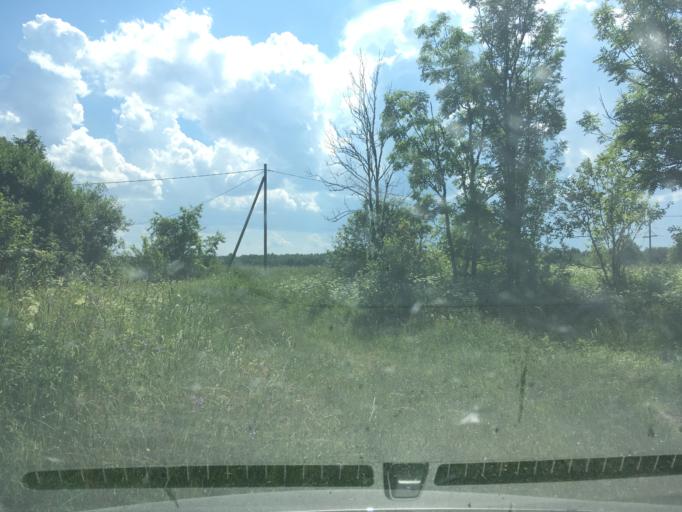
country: EE
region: Raplamaa
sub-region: Maerjamaa vald
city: Marjamaa
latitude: 58.7347
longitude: 24.1615
